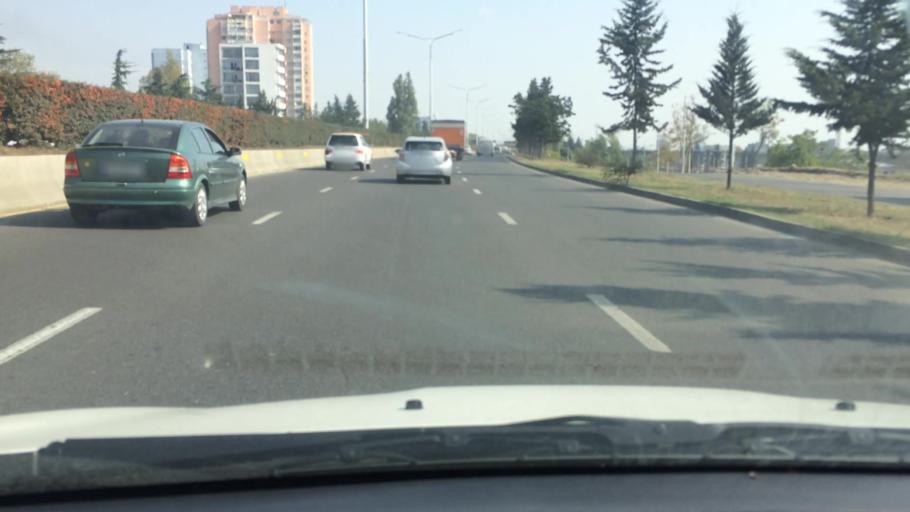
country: GE
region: T'bilisi
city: Tbilisi
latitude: 41.6876
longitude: 44.8499
